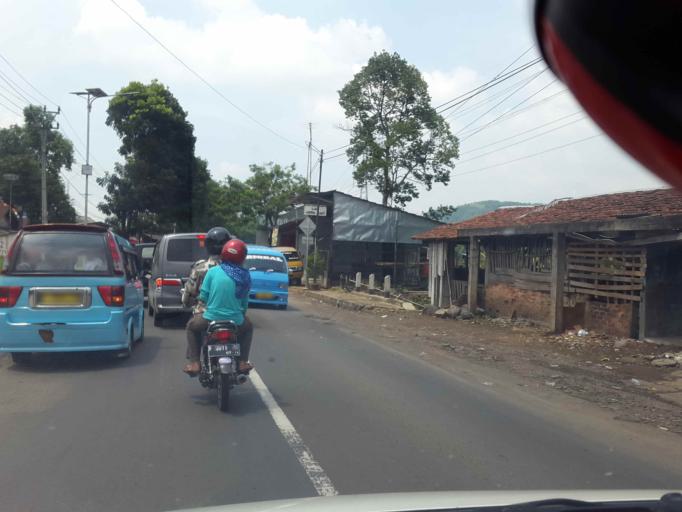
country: ID
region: West Java
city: Sukamaju
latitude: -6.9629
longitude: 106.8783
